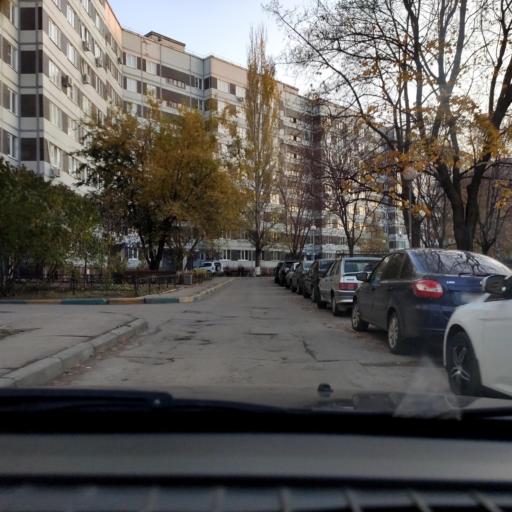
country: RU
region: Samara
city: Tol'yatti
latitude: 53.5305
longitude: 49.3367
